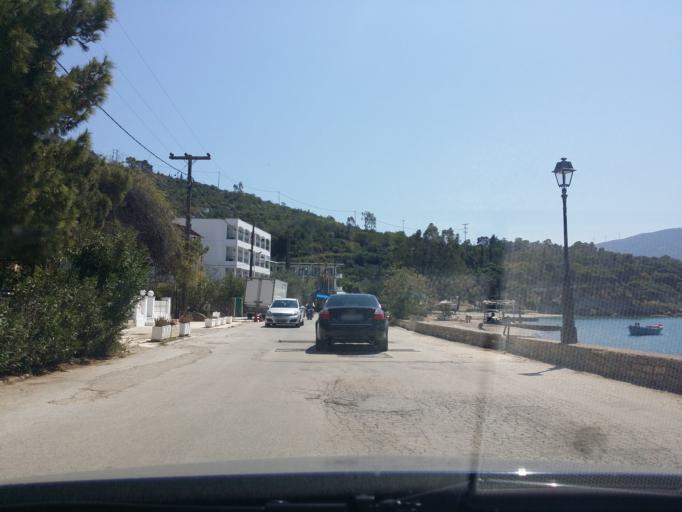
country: GR
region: Attica
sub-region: Nomos Piraios
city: Poros
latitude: 37.5140
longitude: 23.4409
